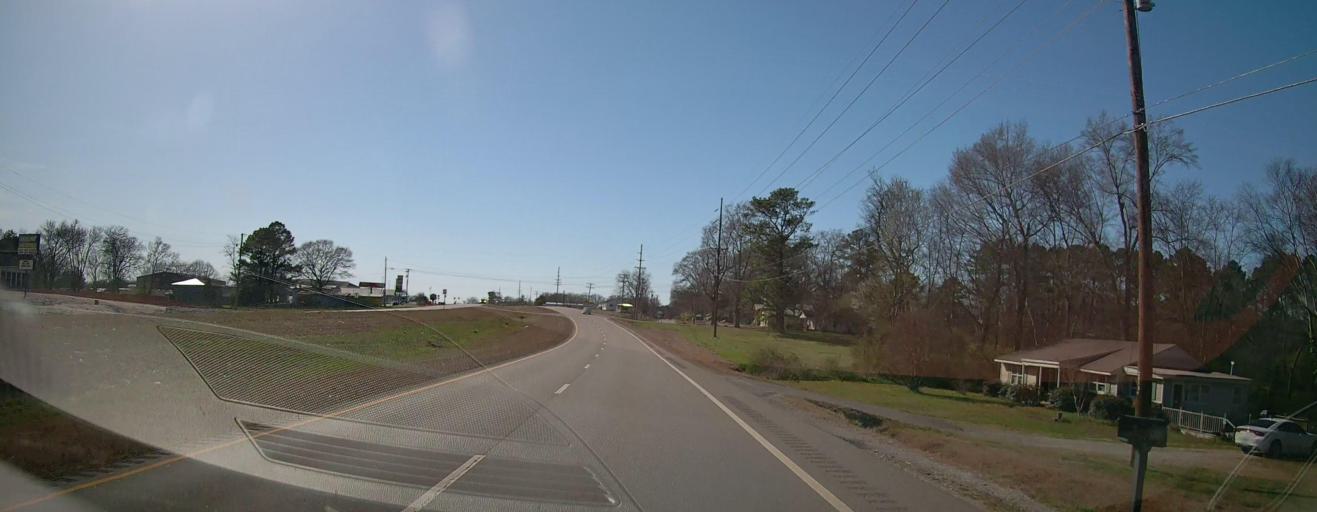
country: US
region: Alabama
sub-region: Lauderdale County
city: Killen
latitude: 34.8615
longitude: -87.4502
